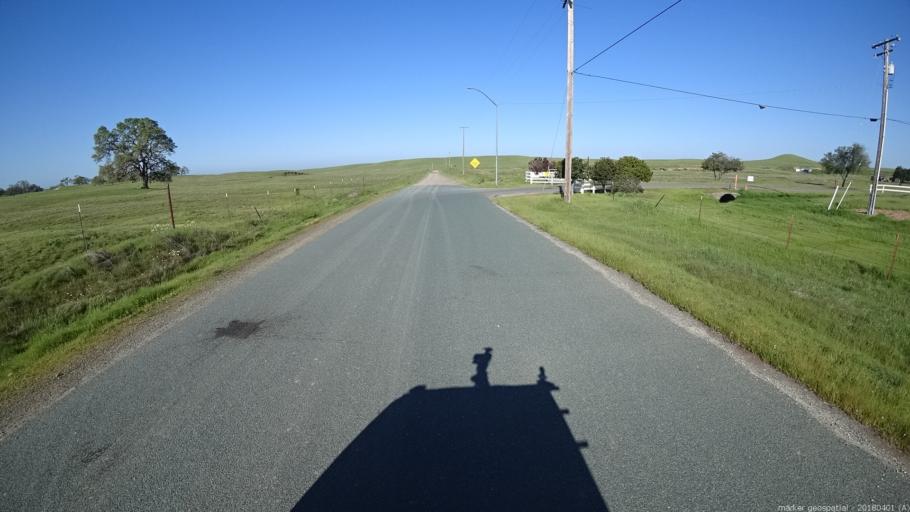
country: US
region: California
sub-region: Sacramento County
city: Rancho Murieta
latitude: 38.4313
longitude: -121.0629
